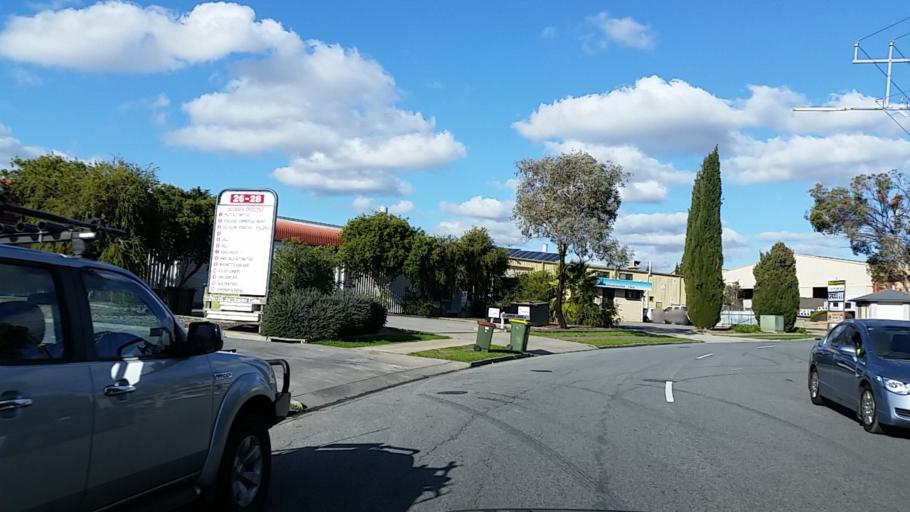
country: AU
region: South Australia
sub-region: Tea Tree Gully
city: Modbury
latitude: -34.8460
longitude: 138.6753
